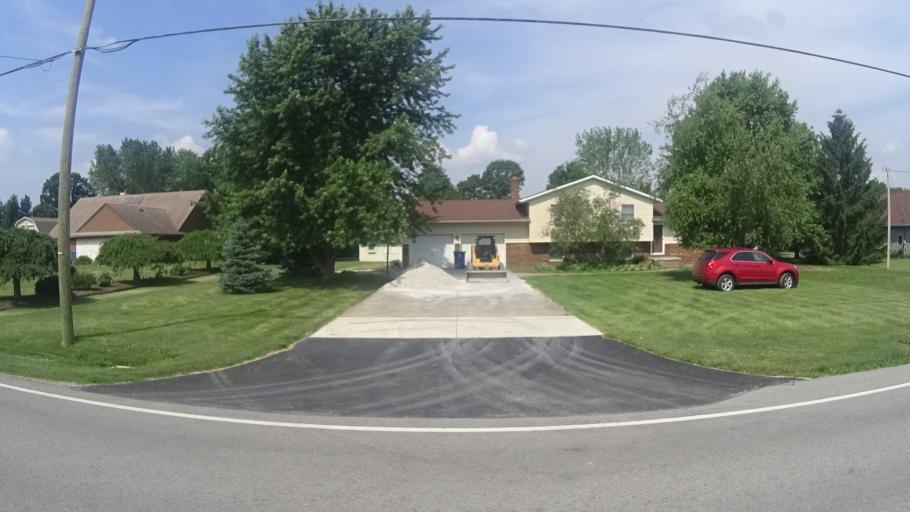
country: US
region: Ohio
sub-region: Erie County
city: Sandusky
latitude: 41.3588
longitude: -82.7278
